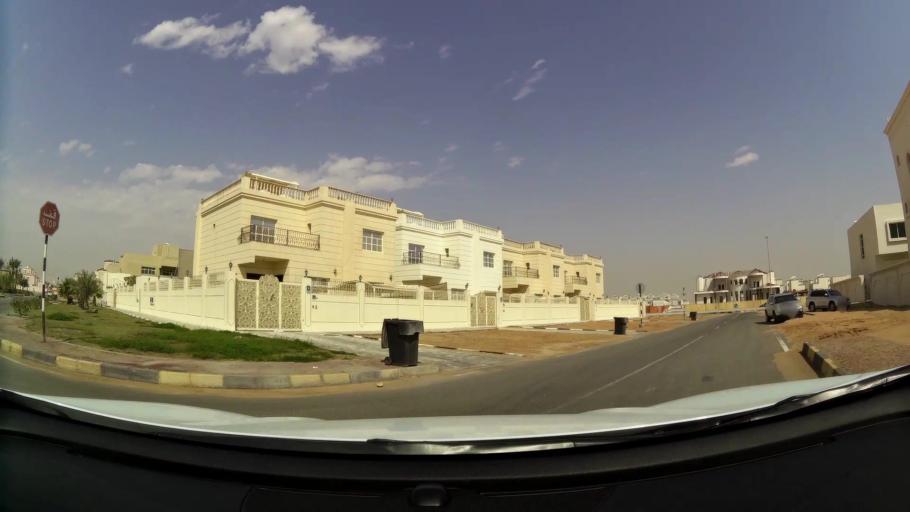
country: AE
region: Abu Dhabi
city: Abu Dhabi
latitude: 24.3354
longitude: 54.5479
